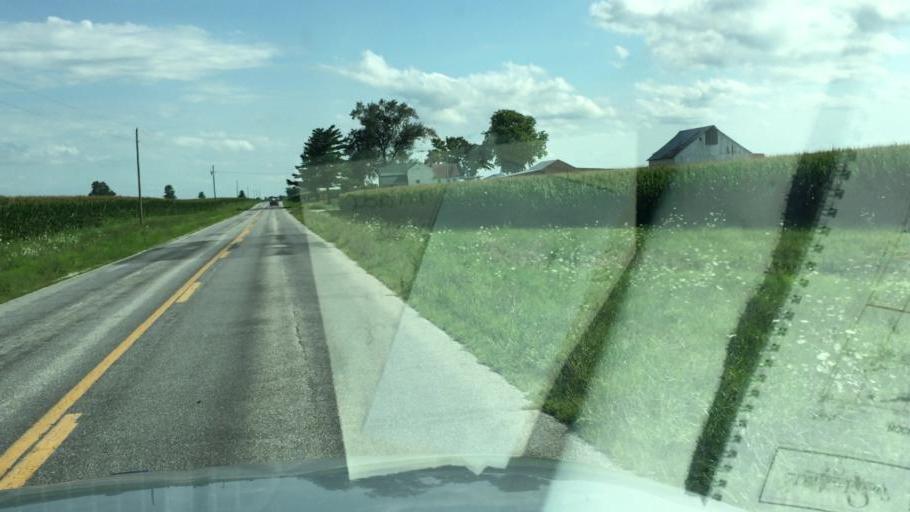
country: US
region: Illinois
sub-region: Hancock County
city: Nauvoo
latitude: 40.5192
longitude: -91.3079
